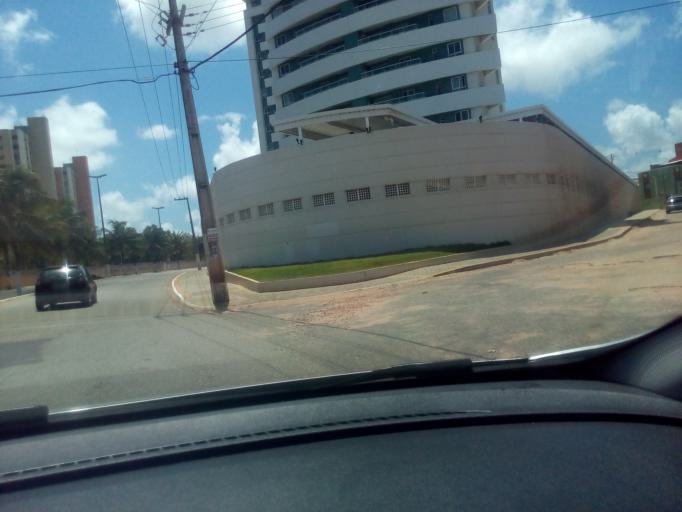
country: BR
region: Rio Grande do Norte
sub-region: Parnamirim
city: Parnamirim
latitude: -5.8937
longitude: -35.1934
